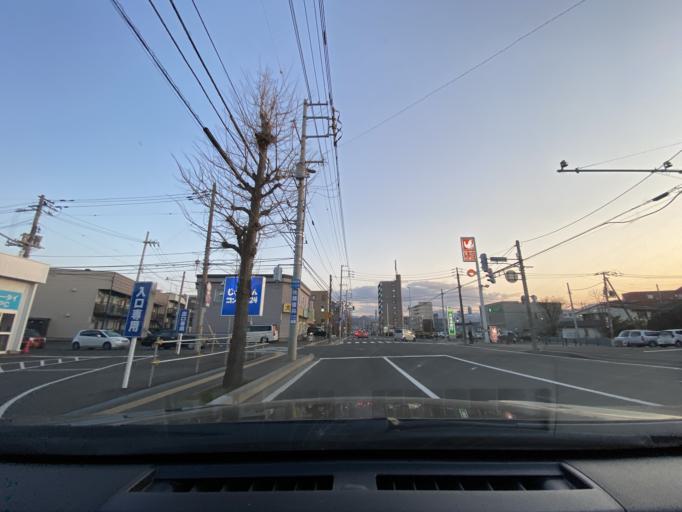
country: JP
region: Hokkaido
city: Sapporo
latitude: 43.0960
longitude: 141.3232
